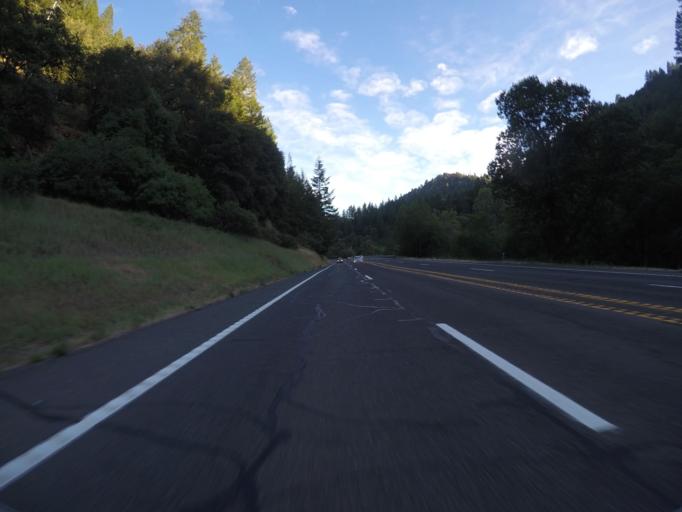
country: US
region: California
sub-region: Mendocino County
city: Laytonville
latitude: 39.5667
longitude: -123.4349
